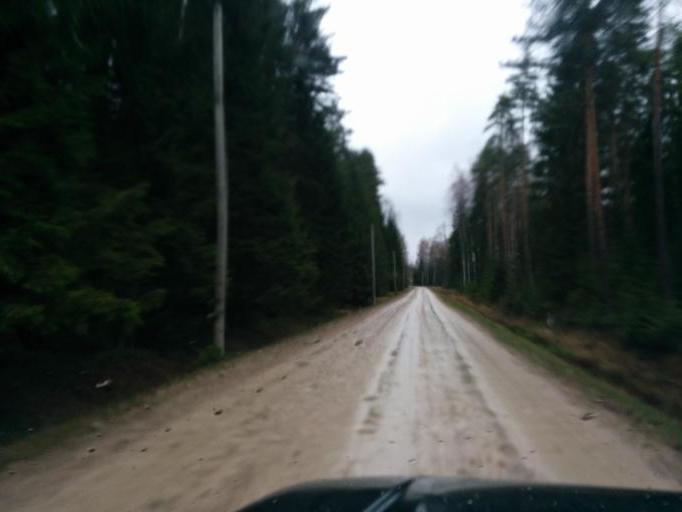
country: LV
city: Tireli
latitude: 56.8255
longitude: 23.7012
